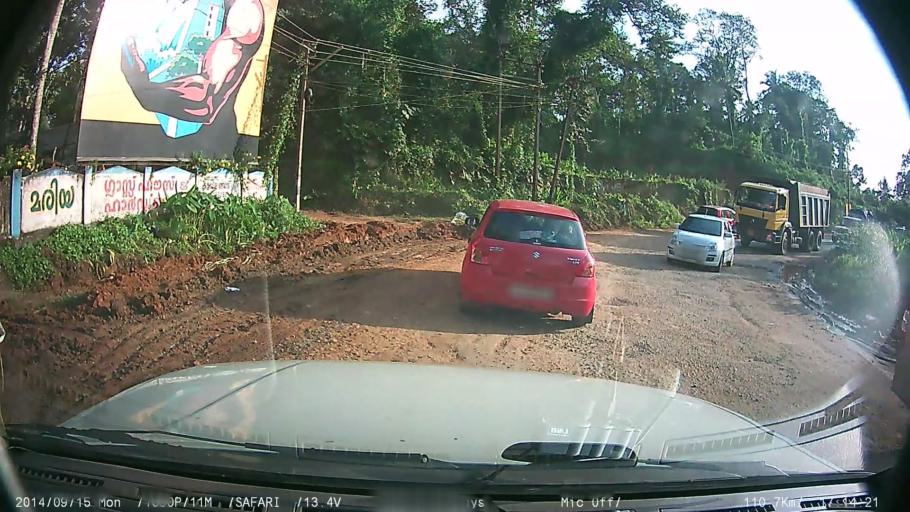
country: IN
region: Kerala
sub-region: Kottayam
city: Palackattumala
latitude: 9.7723
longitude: 76.5720
